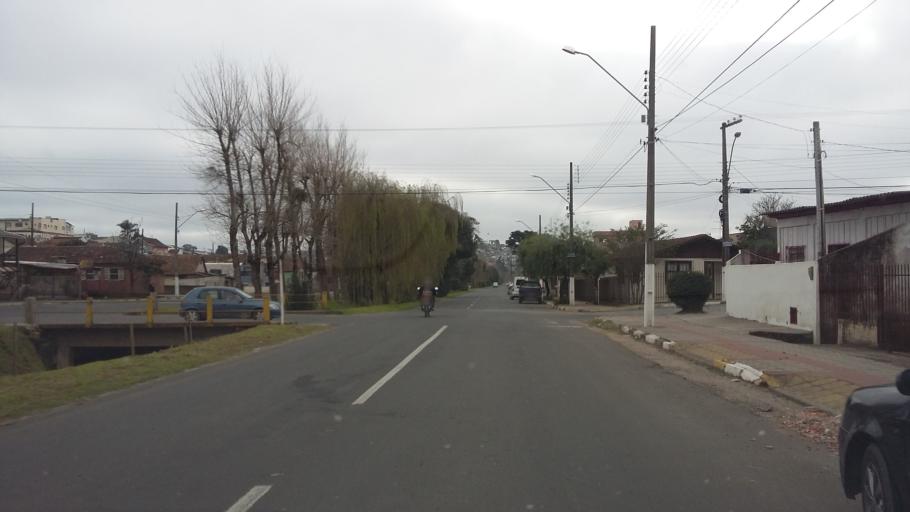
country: BR
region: Santa Catarina
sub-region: Lages
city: Lages
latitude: -27.8214
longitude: -50.3388
